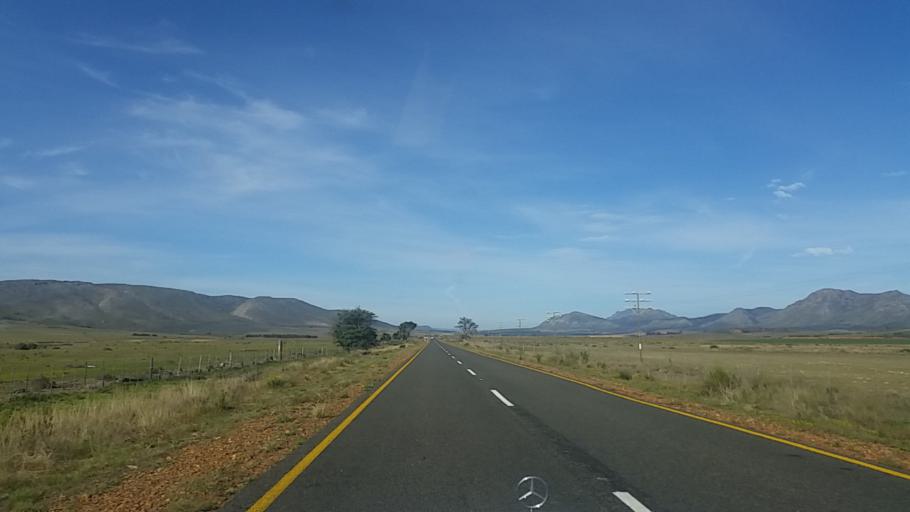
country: ZA
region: Western Cape
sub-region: Eden District Municipality
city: George
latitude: -33.8140
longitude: 22.5249
